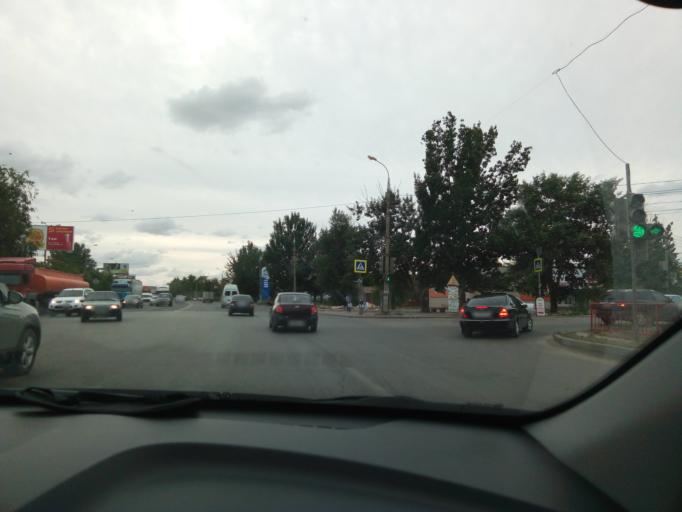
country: RU
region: Volgograd
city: Krasnoslobodsk
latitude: 48.5155
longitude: 44.5348
